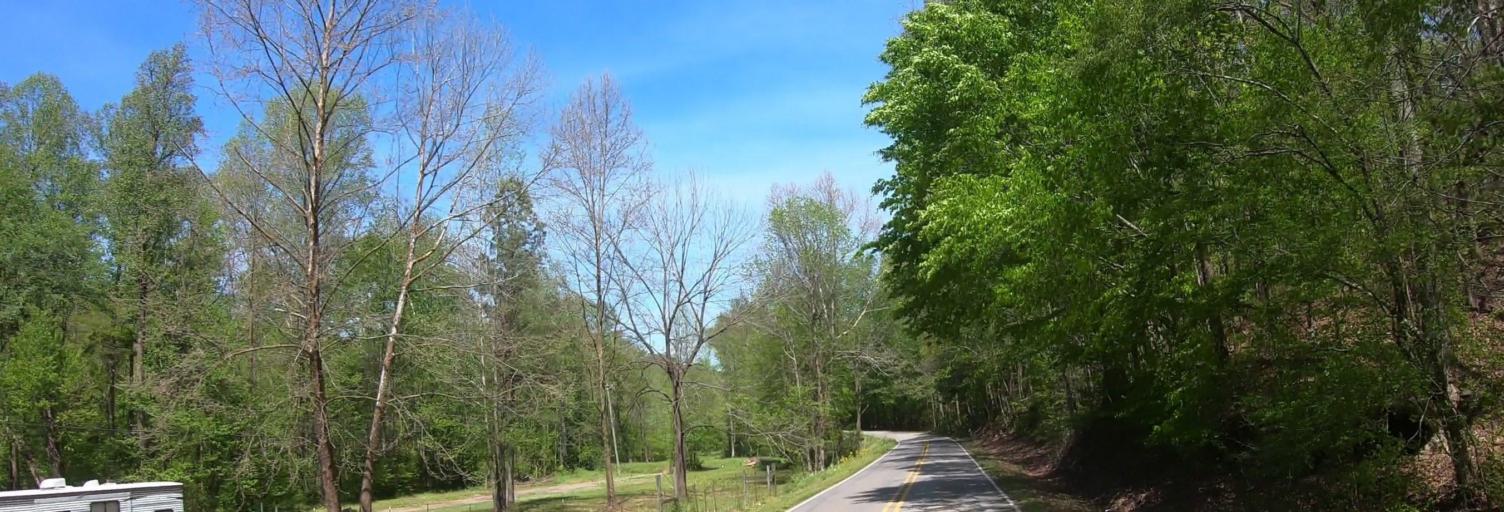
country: US
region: Georgia
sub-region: Bartow County
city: Rydal
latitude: 34.3872
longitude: -84.5913
